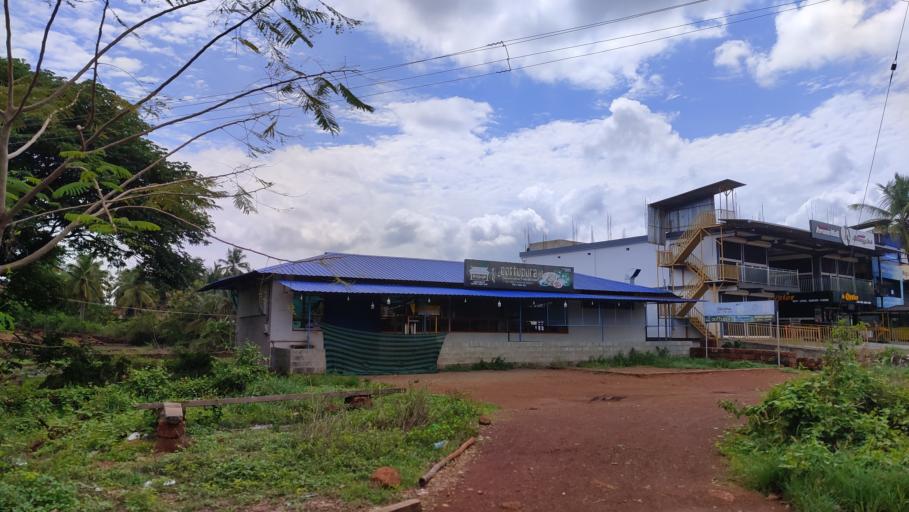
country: IN
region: Kerala
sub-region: Kasaragod District
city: Kannangad
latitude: 12.4012
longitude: 75.0973
